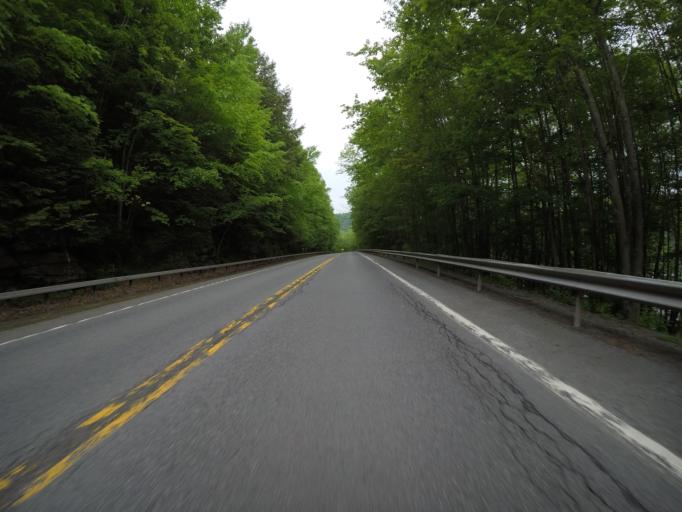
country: US
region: New York
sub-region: Sullivan County
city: Livingston Manor
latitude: 42.0904
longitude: -74.8321
